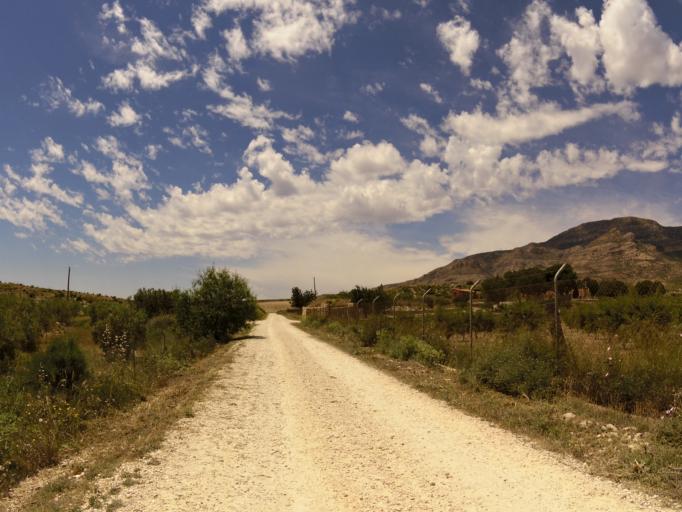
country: ES
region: Valencia
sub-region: Provincia de Alicante
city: Agost
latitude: 38.4457
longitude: -0.6789
